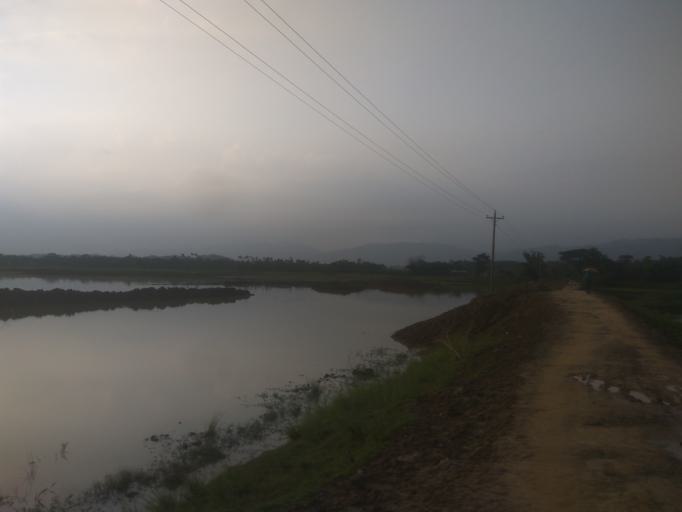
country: IN
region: Assam
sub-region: Karimganj
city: Karimganj
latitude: 24.9954
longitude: 92.4013
